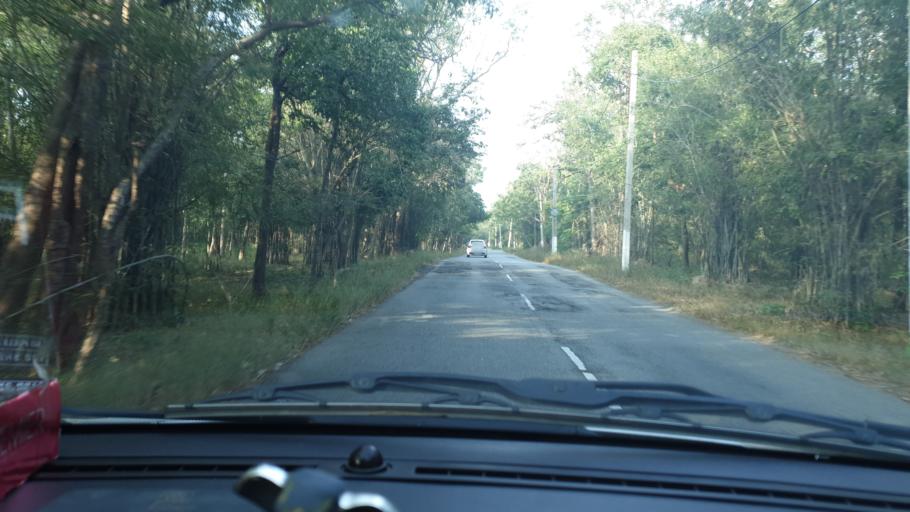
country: IN
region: Andhra Pradesh
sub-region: Kurnool
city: Srisailam
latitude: 16.3008
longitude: 78.7314
